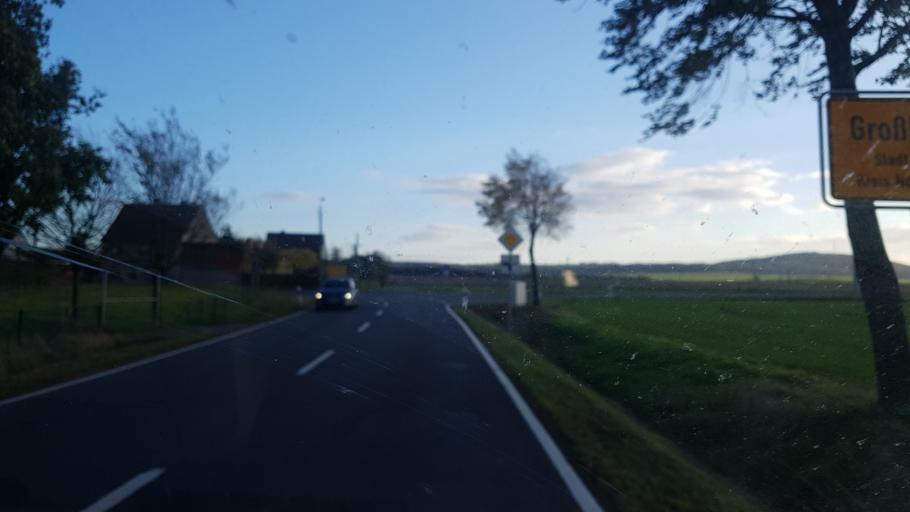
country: DE
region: Saxony
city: Dahlen
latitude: 51.3388
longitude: 13.0301
